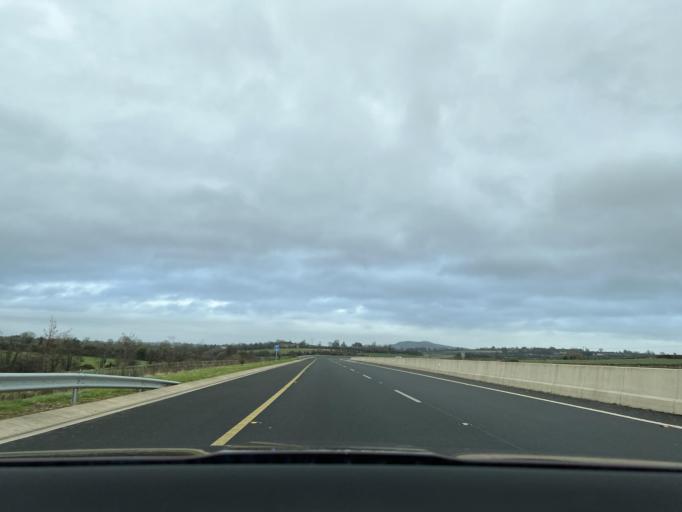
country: IE
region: Leinster
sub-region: Loch Garman
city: Ferns
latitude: 52.5600
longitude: -6.4685
